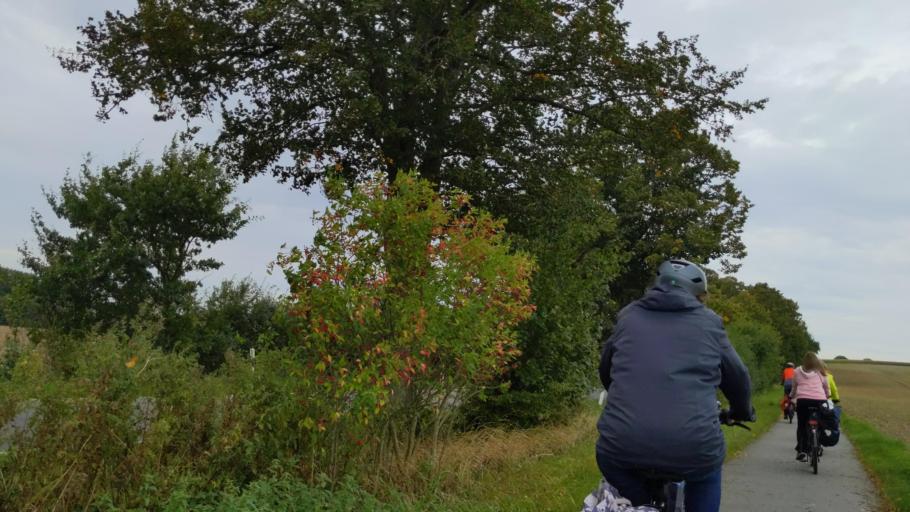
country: DE
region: Mecklenburg-Vorpommern
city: Schlagsdorf
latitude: 53.7624
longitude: 10.8081
